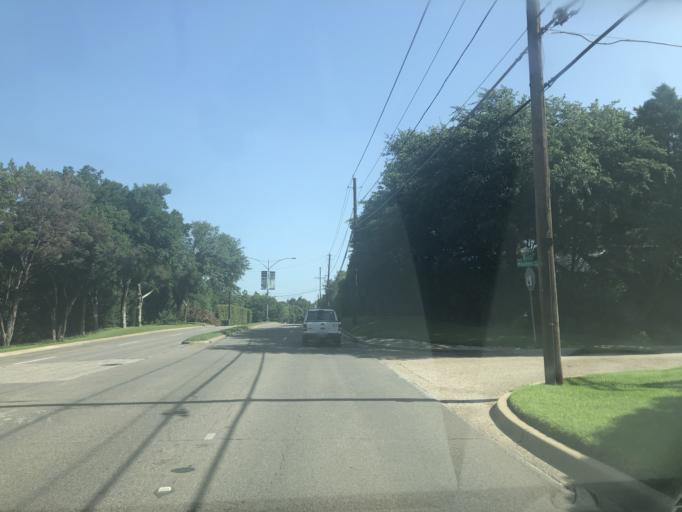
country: US
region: Texas
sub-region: Dallas County
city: University Park
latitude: 32.8849
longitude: -96.8210
